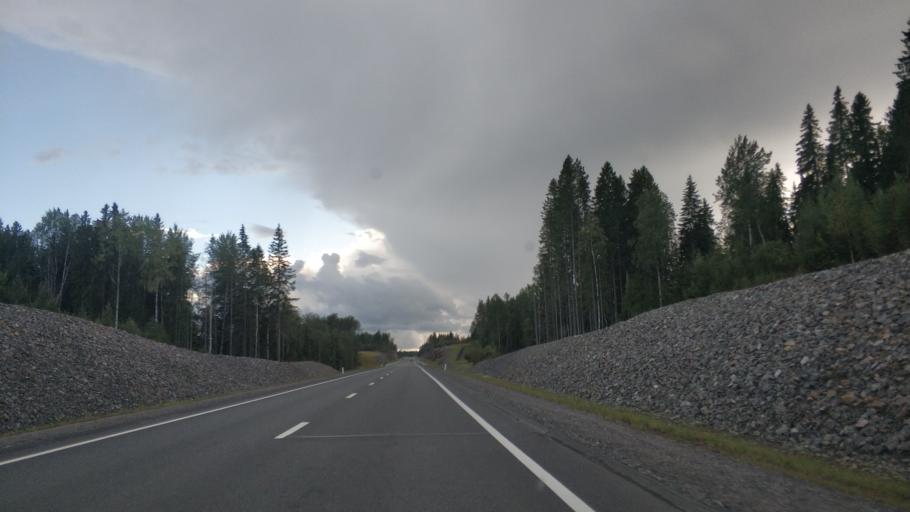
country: RU
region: Republic of Karelia
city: Lakhdenpokh'ya
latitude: 61.4406
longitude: 29.9842
